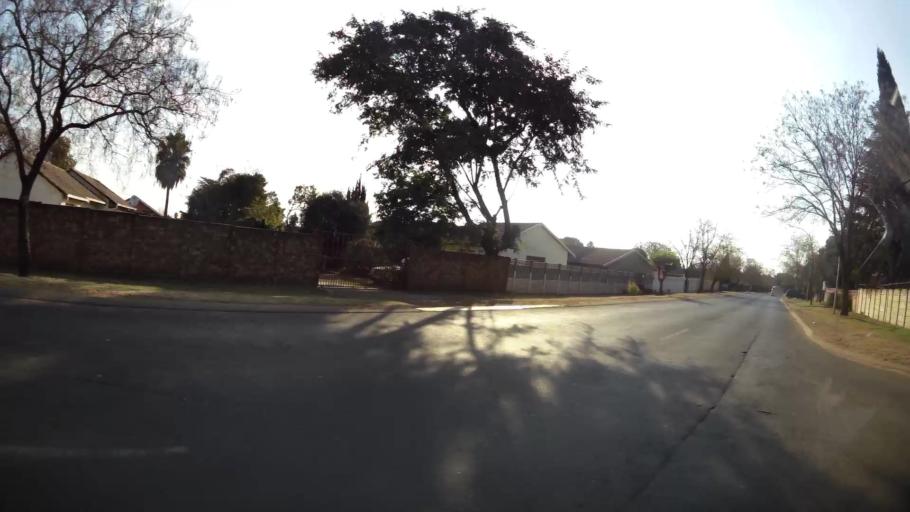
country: ZA
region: Gauteng
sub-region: Ekurhuleni Metropolitan Municipality
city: Benoni
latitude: -26.1345
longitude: 28.3670
